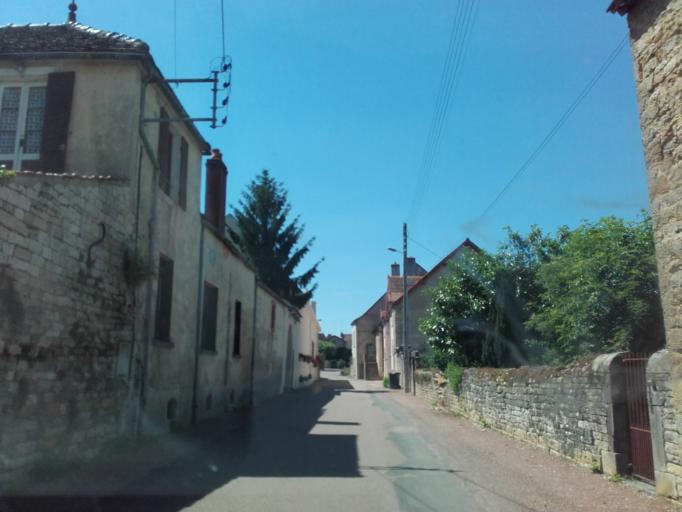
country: FR
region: Bourgogne
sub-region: Departement de Saone-et-Loire
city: Saint-Leger-sur-Dheune
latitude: 46.8950
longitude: 4.6711
